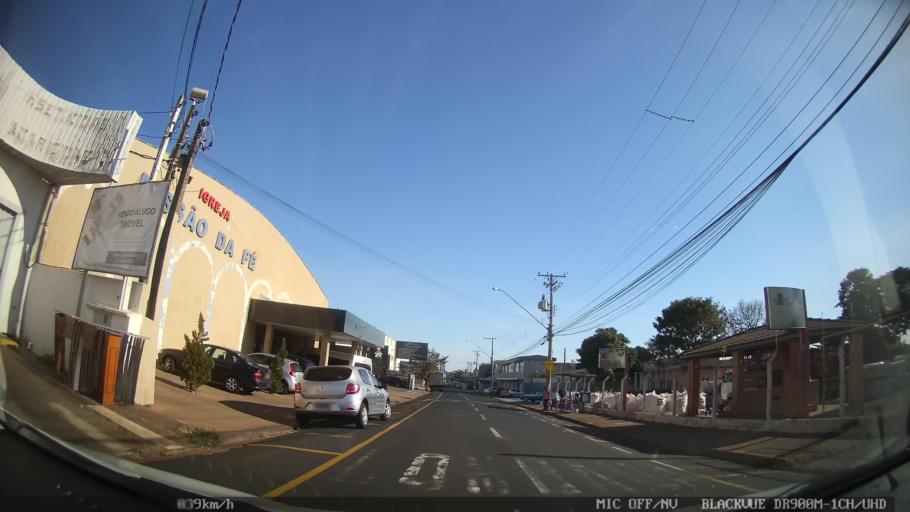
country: BR
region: Sao Paulo
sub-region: Sao Jose Do Rio Preto
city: Sao Jose do Rio Preto
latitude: -20.7922
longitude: -49.3618
